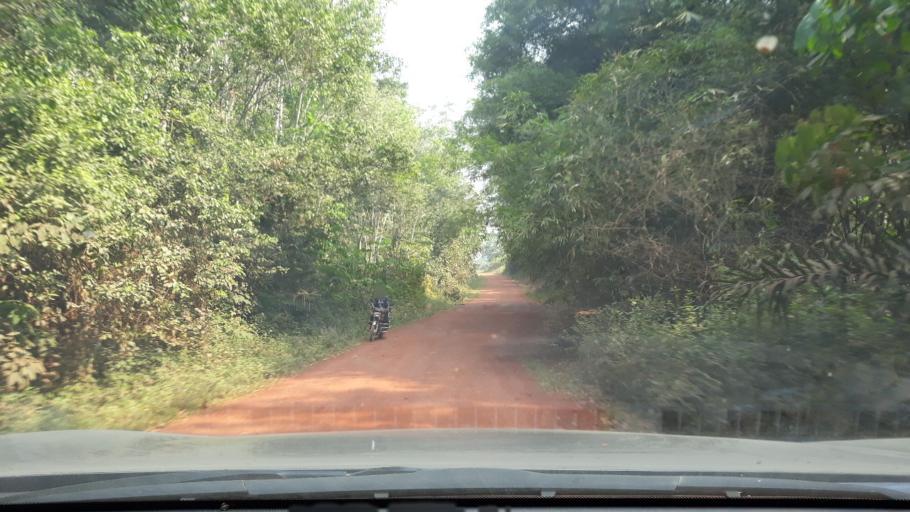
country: CD
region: Eastern Province
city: Kisangani
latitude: 1.2718
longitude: 25.2785
